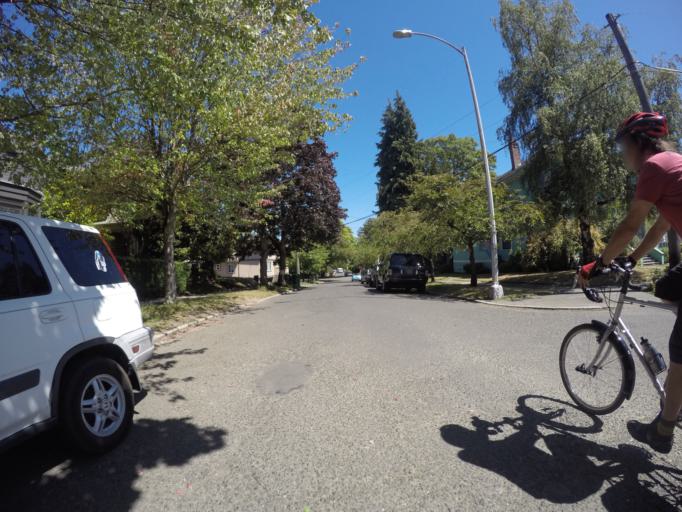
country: US
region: Washington
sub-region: King County
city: Seattle
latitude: 47.6253
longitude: -122.3135
